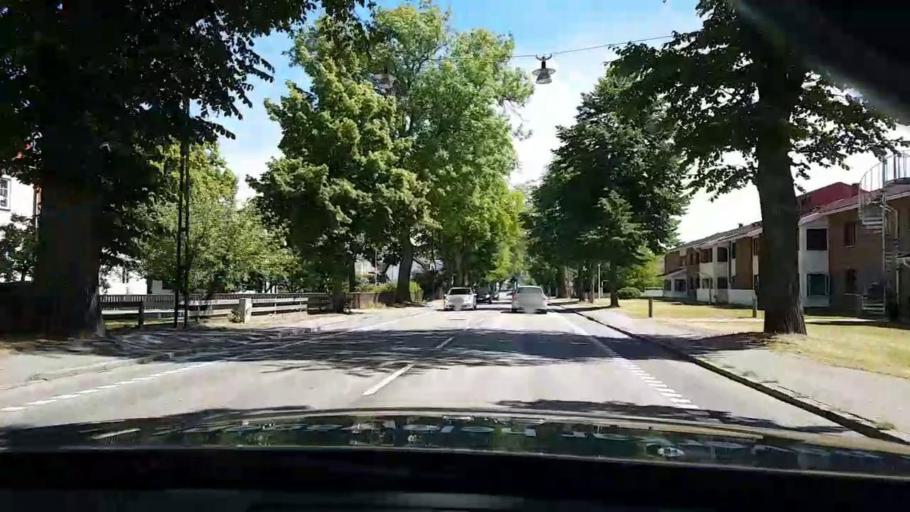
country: SE
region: Kalmar
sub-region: Vasterviks Kommun
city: Vaestervik
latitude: 57.7578
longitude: 16.6249
